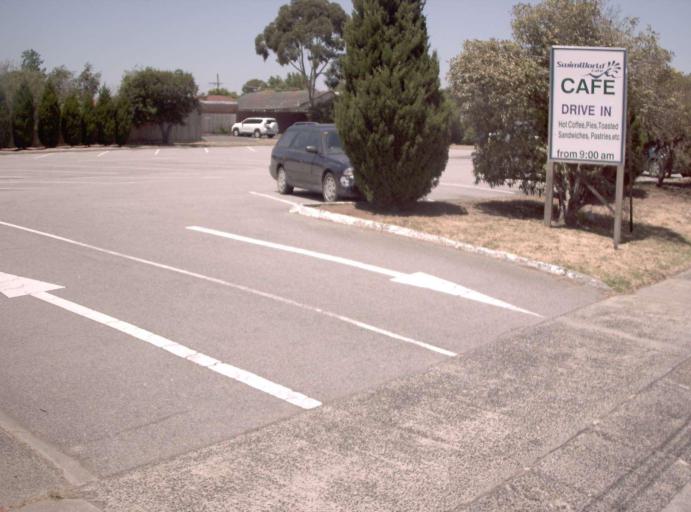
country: AU
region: Victoria
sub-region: Monash
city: Notting Hill
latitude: -37.8952
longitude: 145.1633
